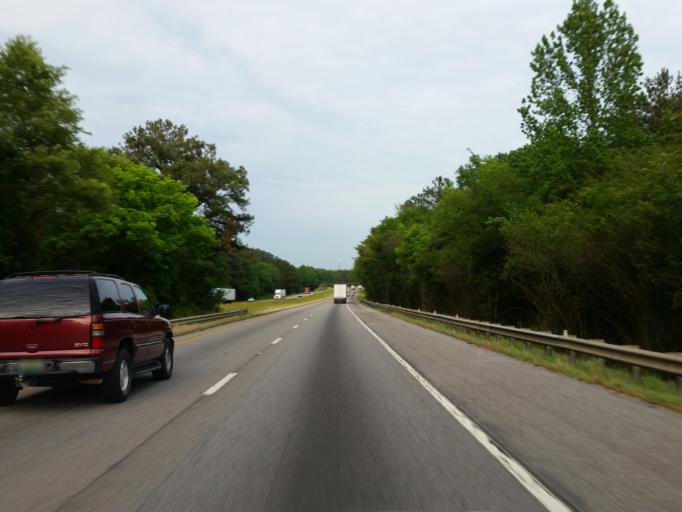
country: US
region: Alabama
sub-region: Talladega County
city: Lincoln
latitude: 33.5886
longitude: -86.0995
